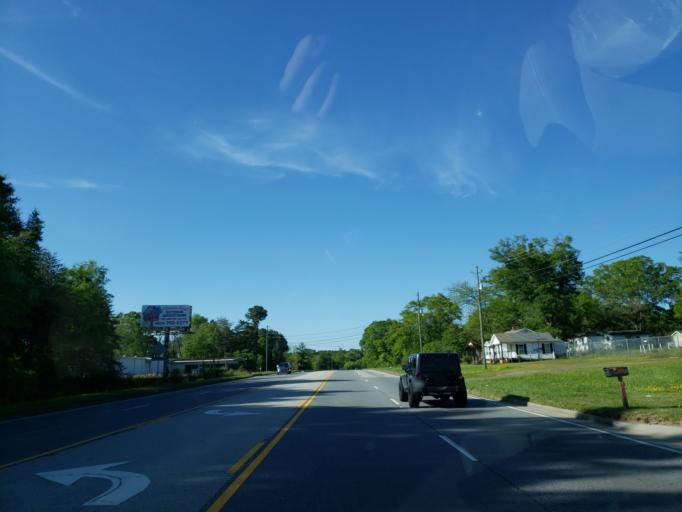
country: US
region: Georgia
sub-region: Polk County
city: Cedartown
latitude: 33.9763
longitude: -85.2579
